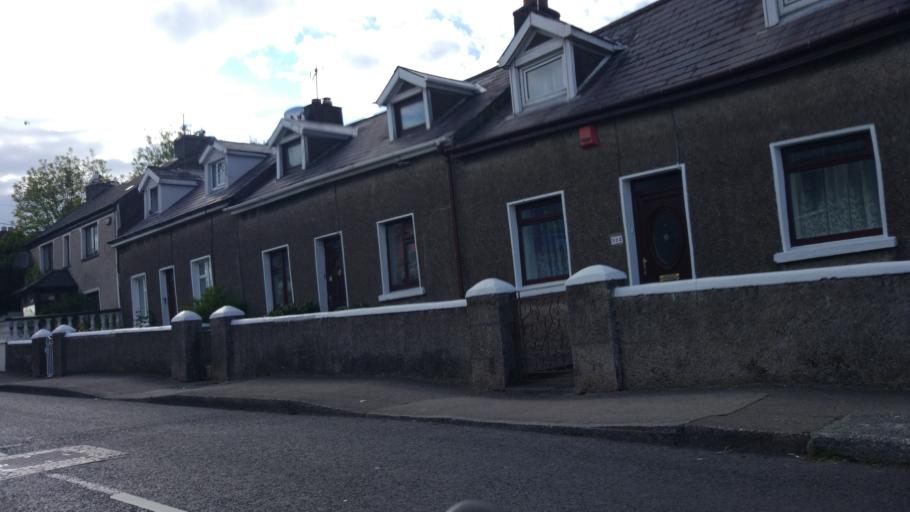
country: IE
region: Munster
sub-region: County Cork
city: Cork
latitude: 51.9137
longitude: -8.4316
